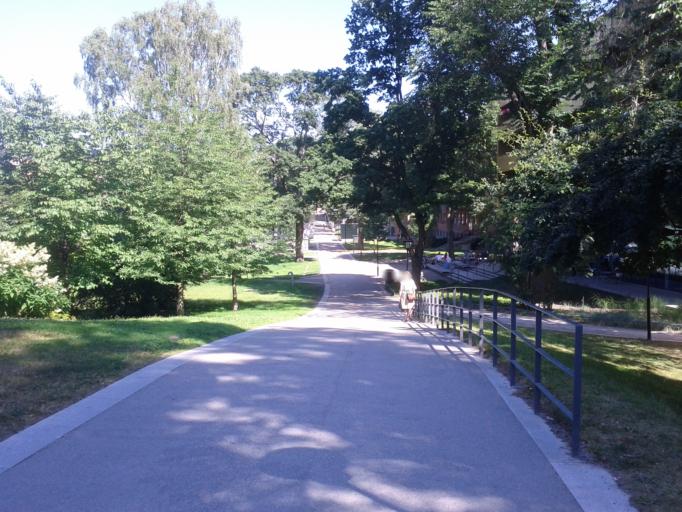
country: SE
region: Stockholm
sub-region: Stockholms Kommun
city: Stockholm
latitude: 59.3397
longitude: 18.0431
